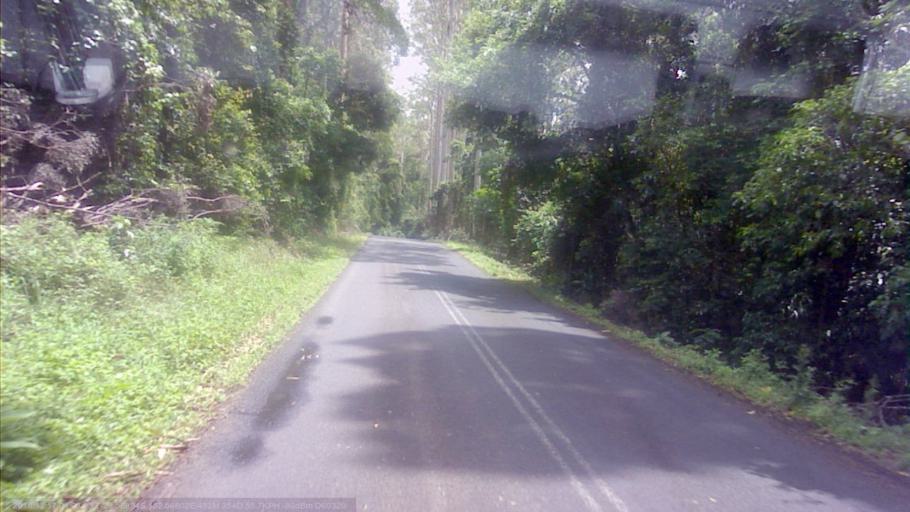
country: AU
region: New South Wales
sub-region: Kyogle
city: Kyogle
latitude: -28.5089
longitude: 152.5680
